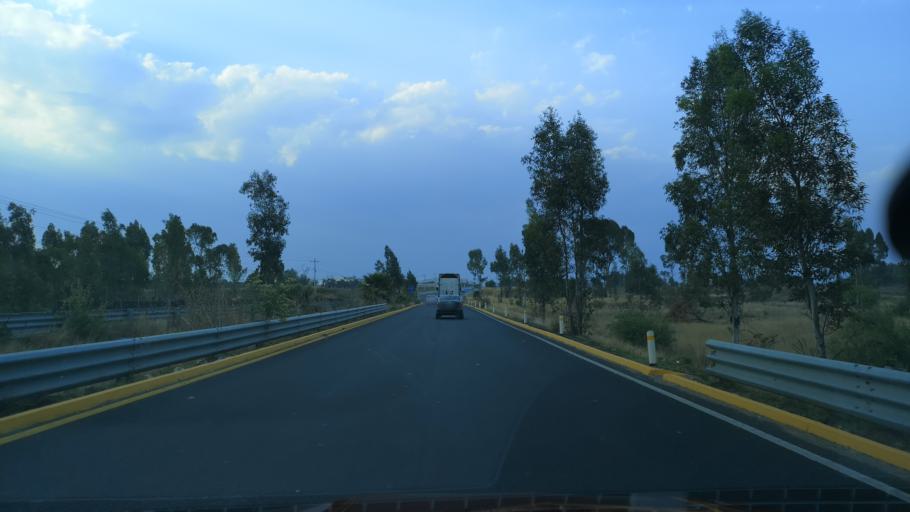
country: MX
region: Puebla
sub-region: Juan C. Bonilla
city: Santa Maria Zacatepec
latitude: 19.1338
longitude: -98.3734
